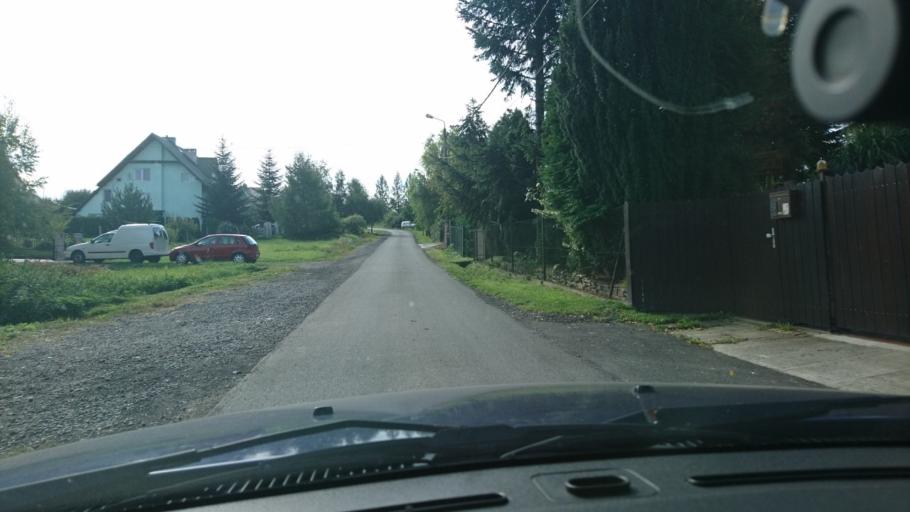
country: PL
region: Silesian Voivodeship
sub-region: Powiat bielski
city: Mazancowice
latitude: 49.8179
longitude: 18.9853
